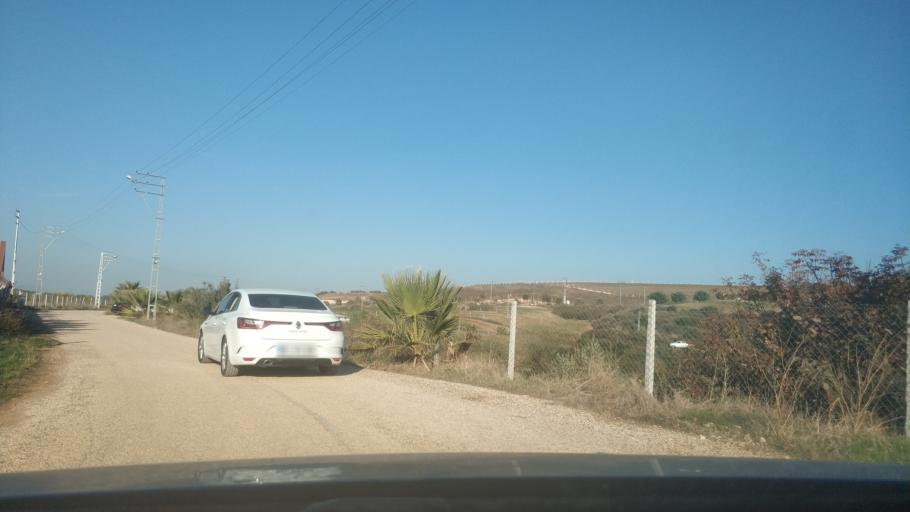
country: TR
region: Adana
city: Adana
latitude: 37.0908
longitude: 35.3033
